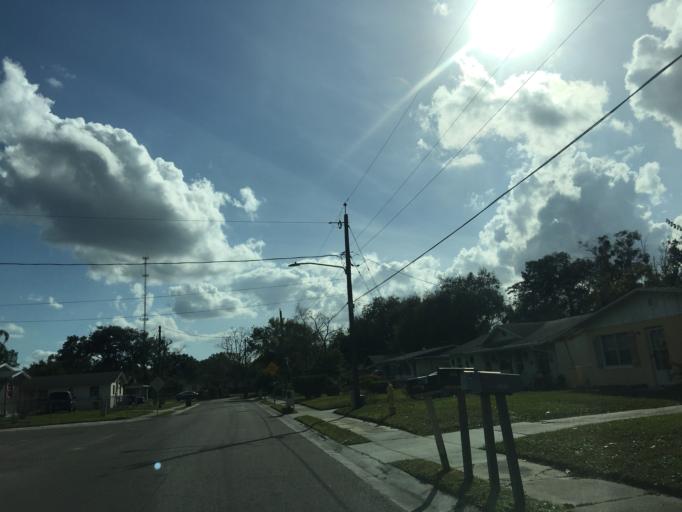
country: US
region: Florida
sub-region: Orange County
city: Eatonville
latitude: 28.6128
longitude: -81.3937
